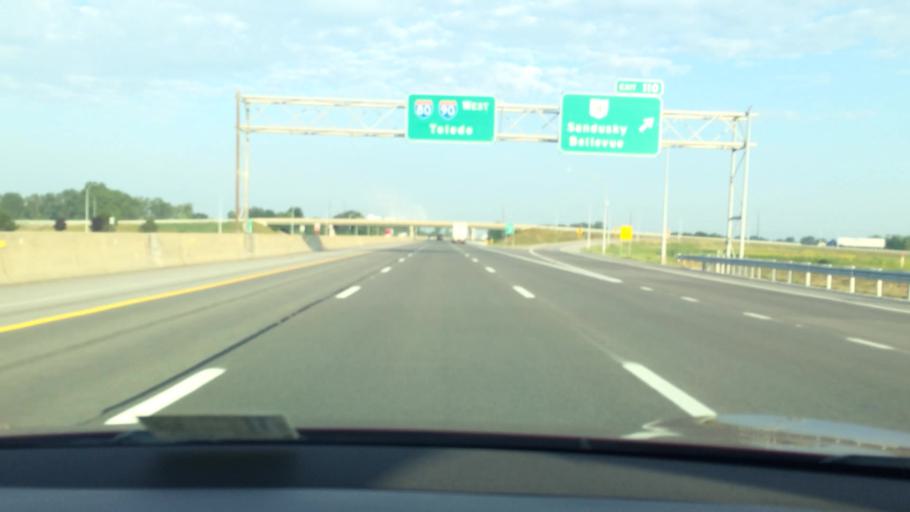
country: US
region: Ohio
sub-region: Huron County
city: Bellevue
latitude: 41.3406
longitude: -82.7620
